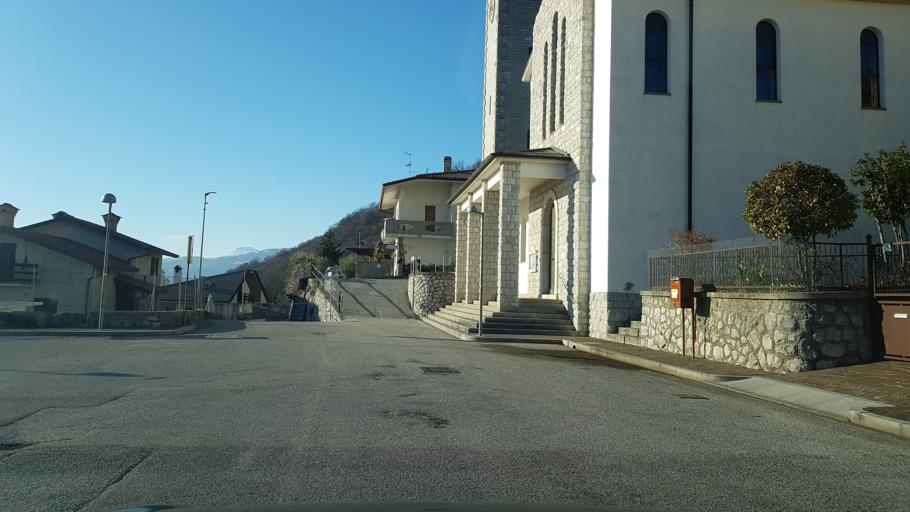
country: IT
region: Friuli Venezia Giulia
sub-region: Provincia di Udine
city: Forgaria nel Friuli
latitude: 46.2270
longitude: 12.9997
